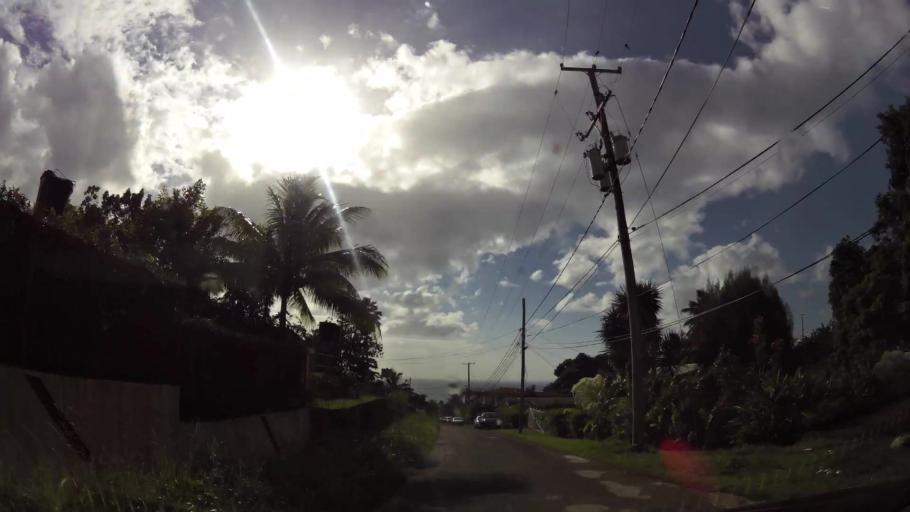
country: DM
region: Saint George
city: Roseau
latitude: 15.3066
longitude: -61.3721
